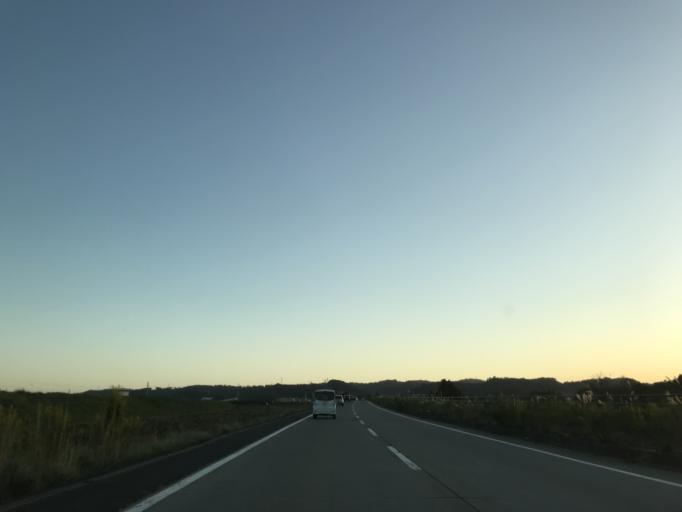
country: JP
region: Iwate
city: Ichinoseki
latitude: 38.9817
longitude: 141.1227
